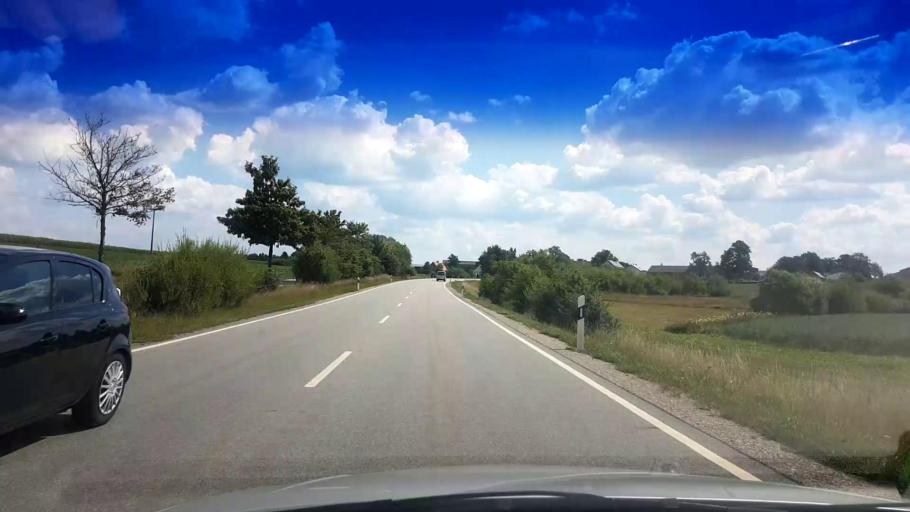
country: DE
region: Bavaria
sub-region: Upper Palatinate
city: Tirschenreuth
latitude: 49.8731
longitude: 12.2852
